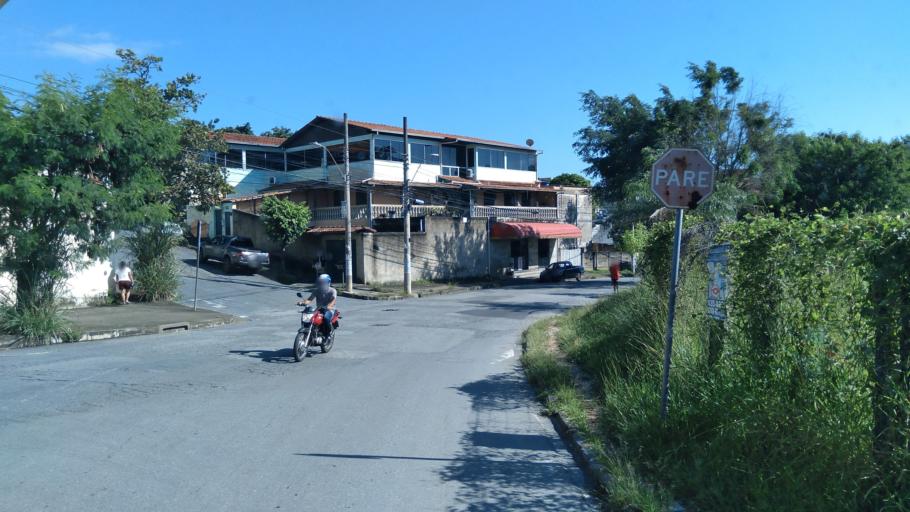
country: BR
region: Minas Gerais
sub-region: Santa Luzia
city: Santa Luzia
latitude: -19.8260
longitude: -43.8984
